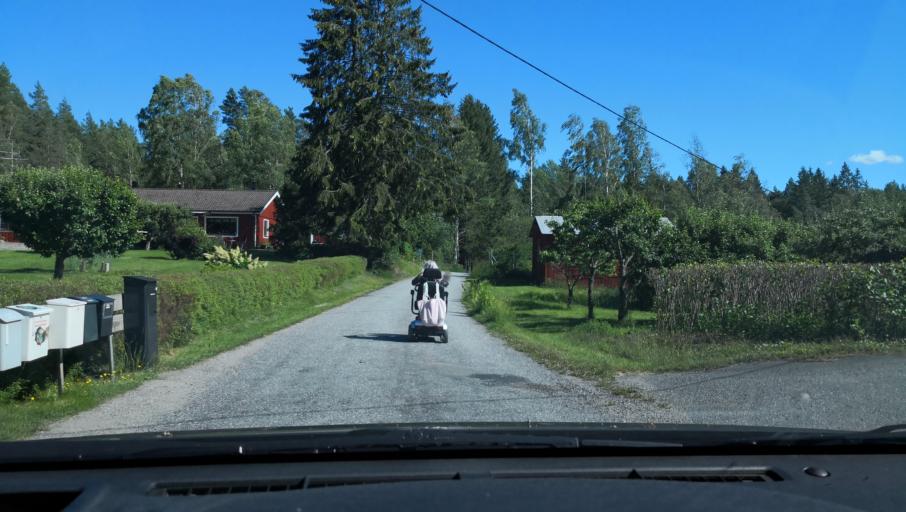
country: SE
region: Soedermanland
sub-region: Eskilstuna Kommun
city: Eskilstuna
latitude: 59.3423
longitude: 16.5617
